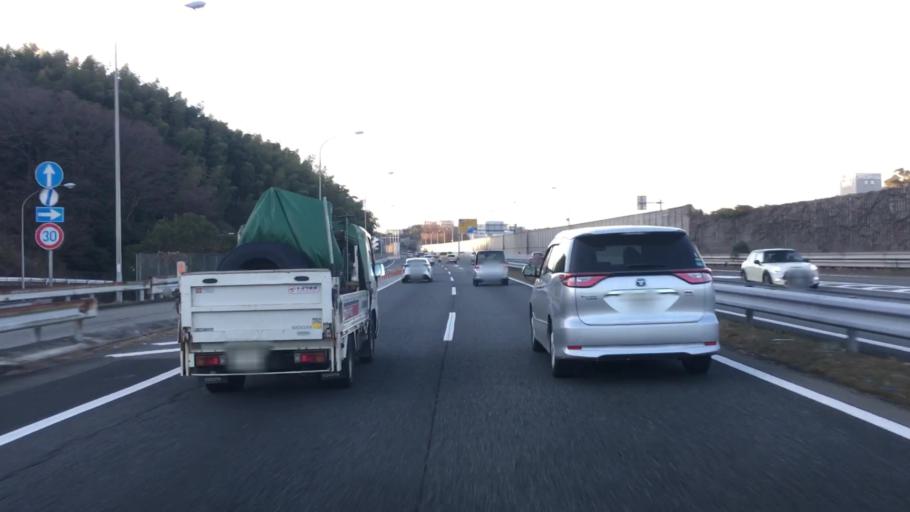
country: JP
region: Kanagawa
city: Kamakura
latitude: 35.3835
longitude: 139.5831
